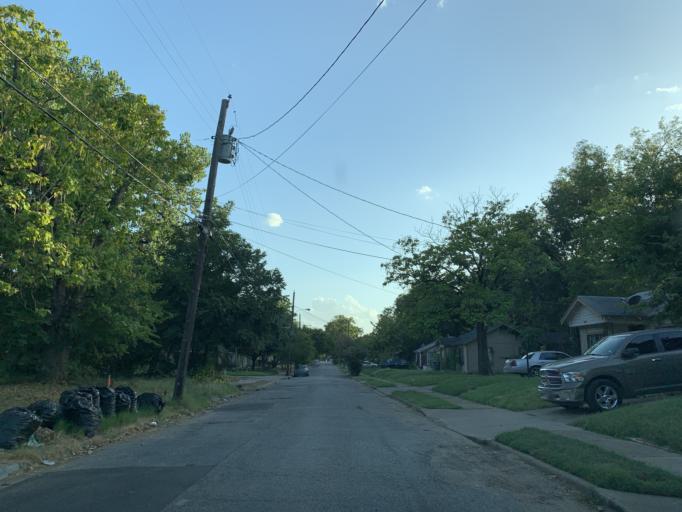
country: US
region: Texas
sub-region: Dallas County
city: Dallas
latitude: 32.7646
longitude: -96.7441
